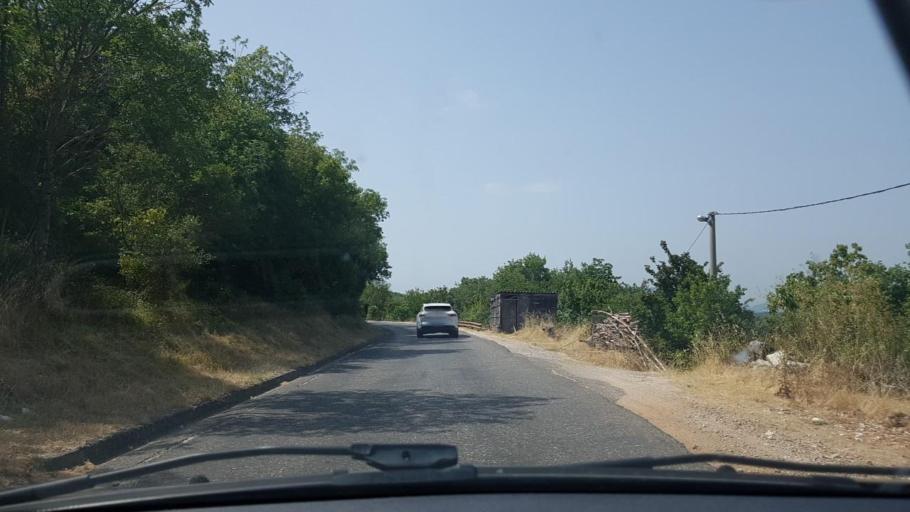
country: BA
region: Federation of Bosnia and Herzegovina
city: Tasovcici
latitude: 43.0352
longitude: 17.7250
